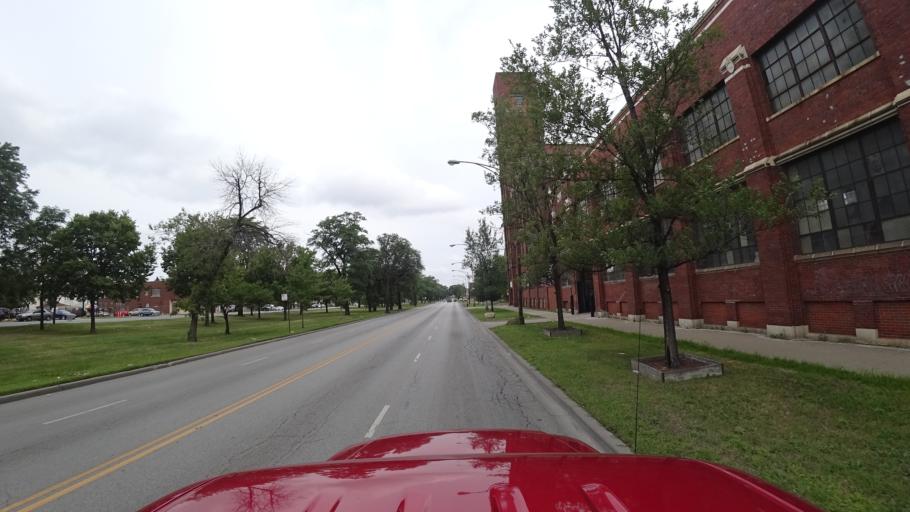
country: US
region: Illinois
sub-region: Cook County
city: Chicago
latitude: 41.8132
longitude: -87.6840
